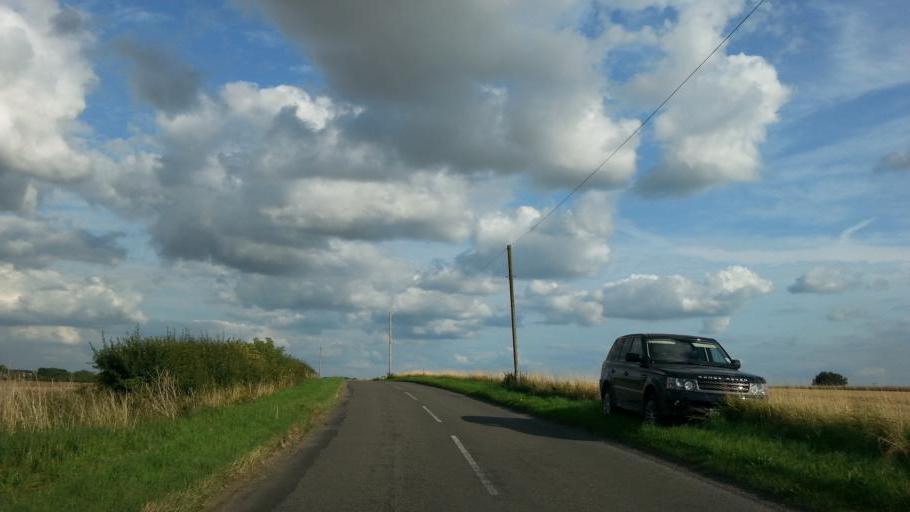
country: GB
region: England
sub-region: Nottinghamshire
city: Farndon
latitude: 53.0091
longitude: -0.8481
